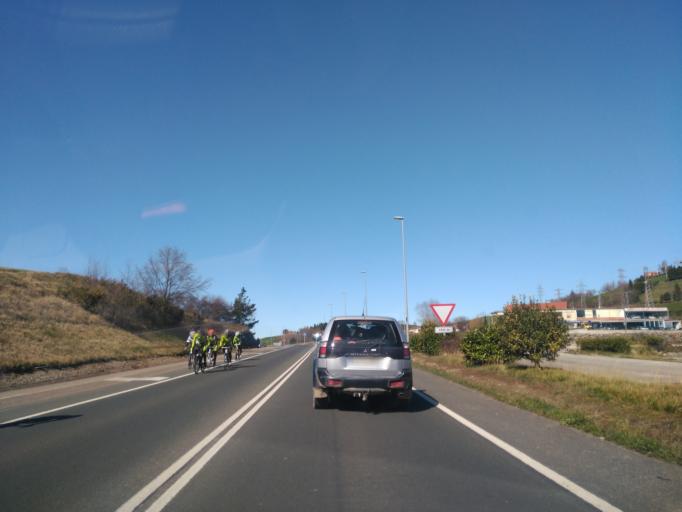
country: ES
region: Cantabria
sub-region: Provincia de Cantabria
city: Cabezon de la Sal
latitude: 43.3099
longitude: -4.2430
